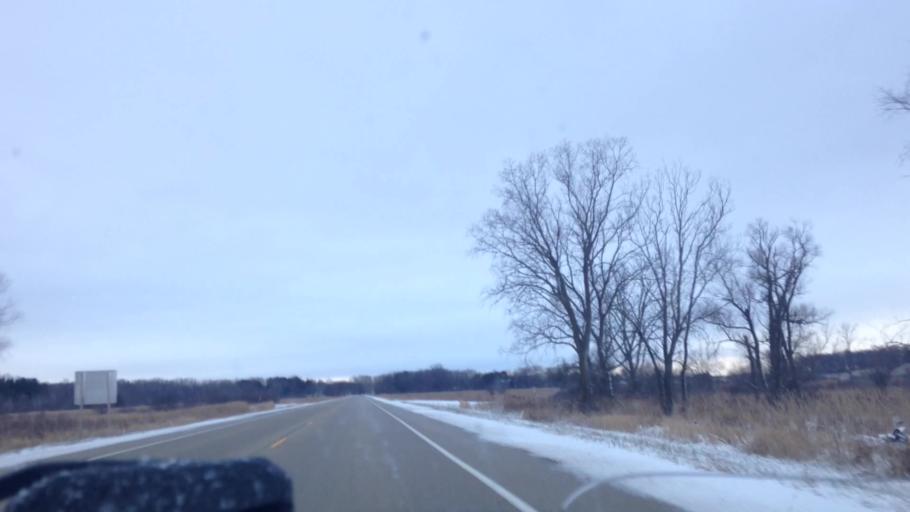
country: US
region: Wisconsin
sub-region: Dodge County
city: Horicon
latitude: 43.4674
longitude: -88.6082
